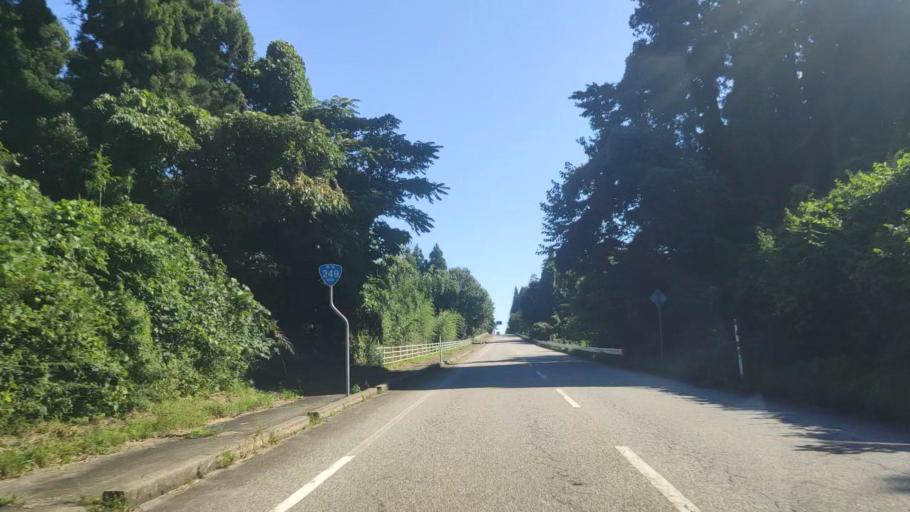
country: JP
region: Ishikawa
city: Nanao
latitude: 37.3730
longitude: 137.2350
